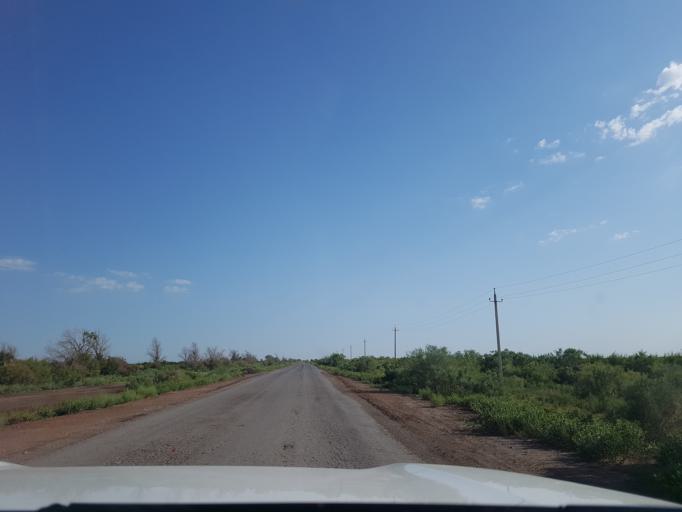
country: TM
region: Dasoguz
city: Koeneuergench
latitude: 41.8834
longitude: 58.7065
